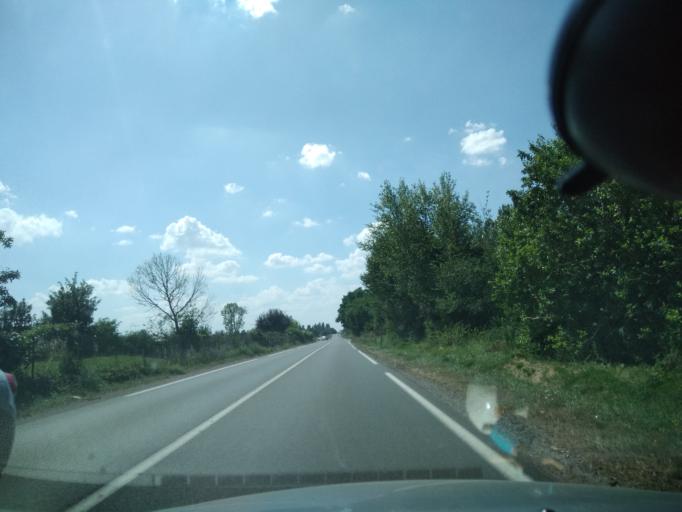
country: FR
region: Centre
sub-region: Departement d'Indre-et-Loire
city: Saint-Pierre-des-Corps
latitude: 47.3811
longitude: 0.7470
